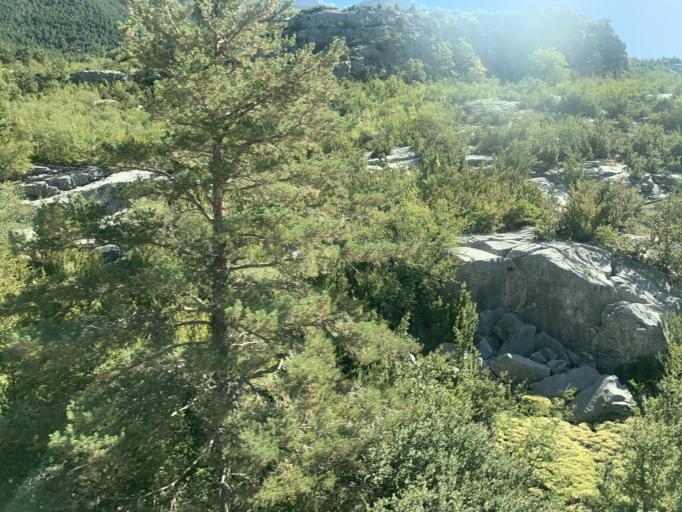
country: ES
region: Aragon
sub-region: Provincia de Huesca
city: Broto
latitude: 42.6527
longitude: -0.1006
